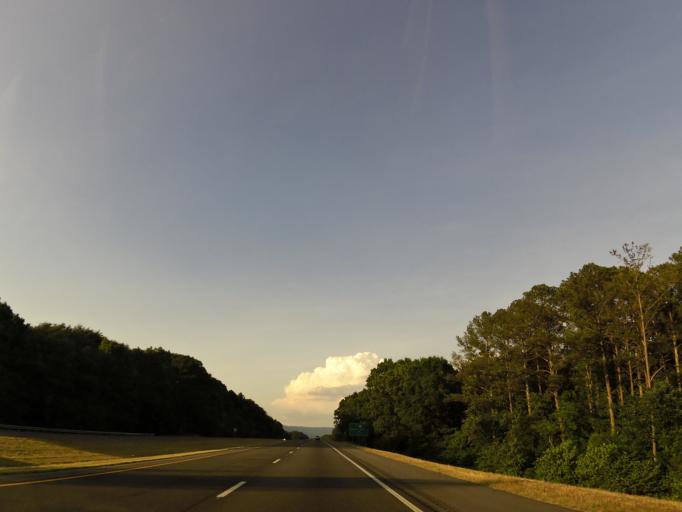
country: US
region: Georgia
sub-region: Dade County
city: Trenton
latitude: 34.6882
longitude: -85.5769
